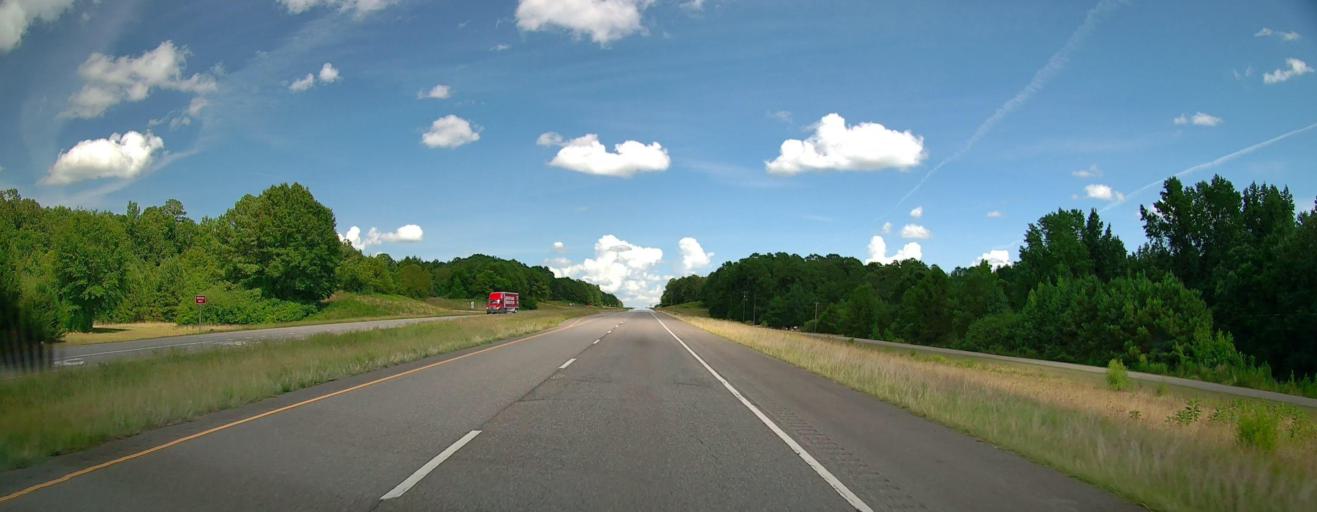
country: US
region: Alabama
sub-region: Pickens County
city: Reform
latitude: 33.4007
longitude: -88.0674
